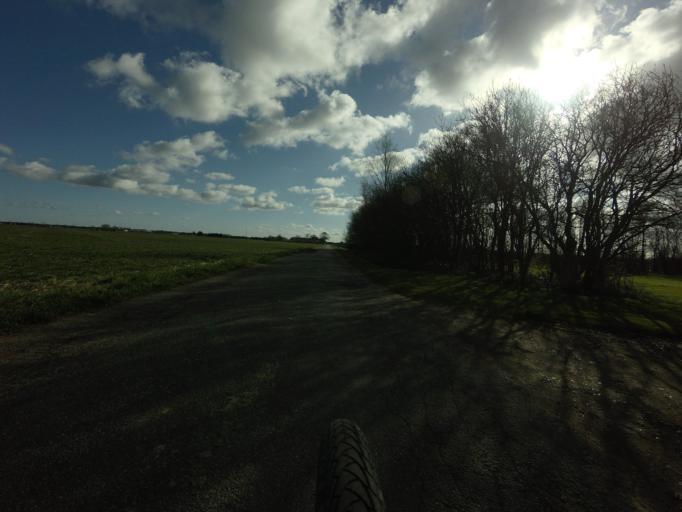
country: DK
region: North Denmark
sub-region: Hjorring Kommune
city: Vra
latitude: 57.3208
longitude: 9.9114
